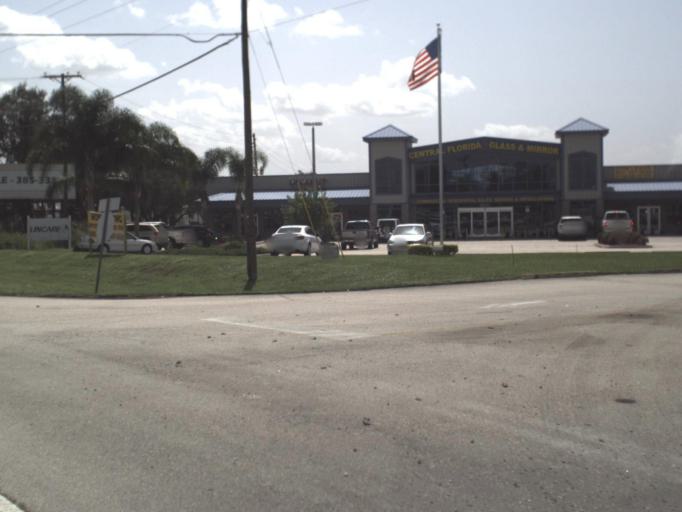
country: US
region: Florida
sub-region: Highlands County
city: Sebring
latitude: 27.4590
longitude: -81.4279
